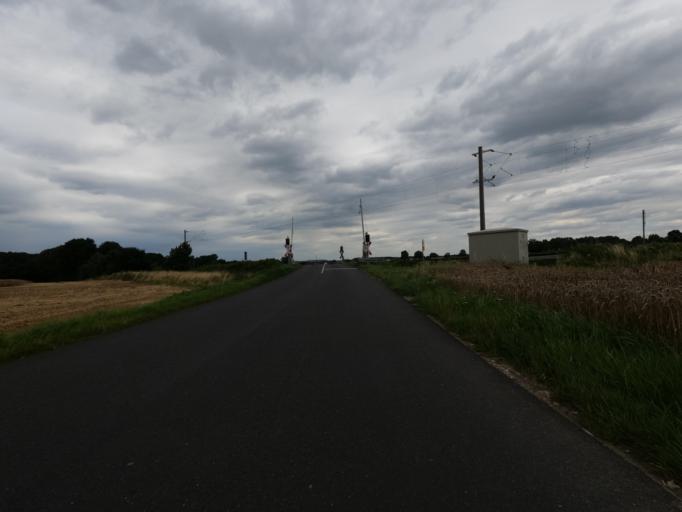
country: DE
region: North Rhine-Westphalia
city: Huckelhoven
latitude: 51.0074
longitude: 6.1874
